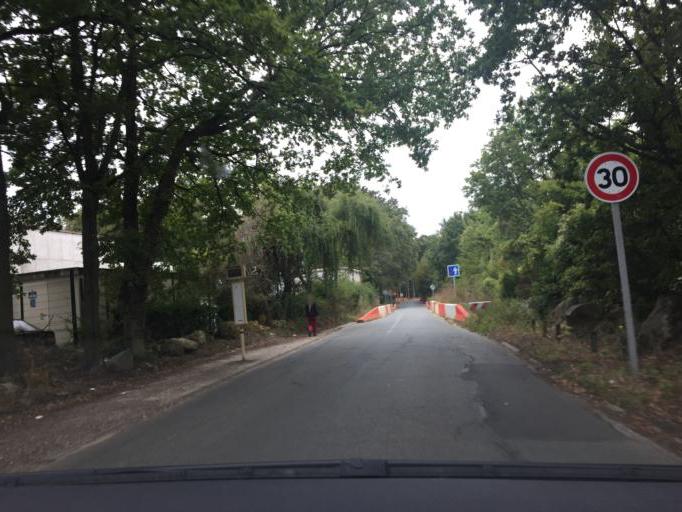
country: FR
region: Ile-de-France
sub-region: Departement de l'Essonne
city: Bures-sur-Yvette
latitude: 48.7079
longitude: 2.1759
